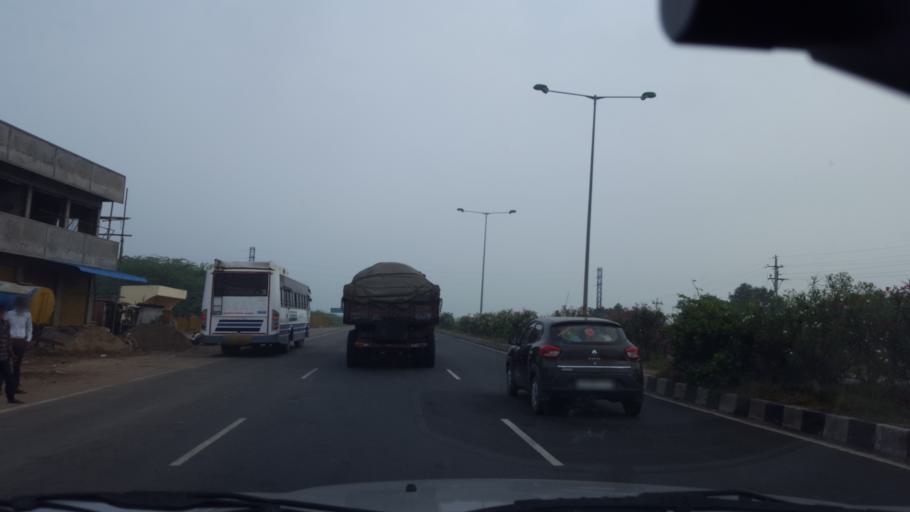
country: IN
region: Andhra Pradesh
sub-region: Prakasam
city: Ongole
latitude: 15.6375
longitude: 80.0162
